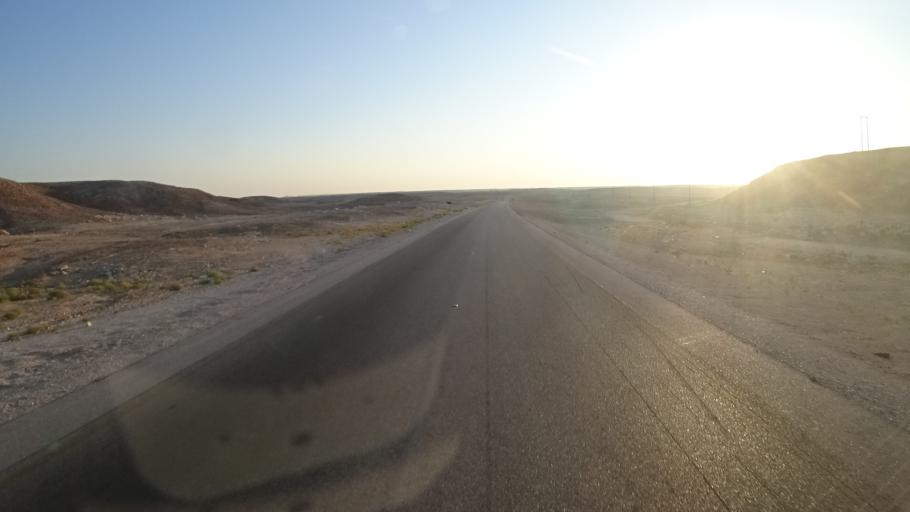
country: OM
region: Zufar
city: Salalah
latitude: 17.5323
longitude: 53.4033
